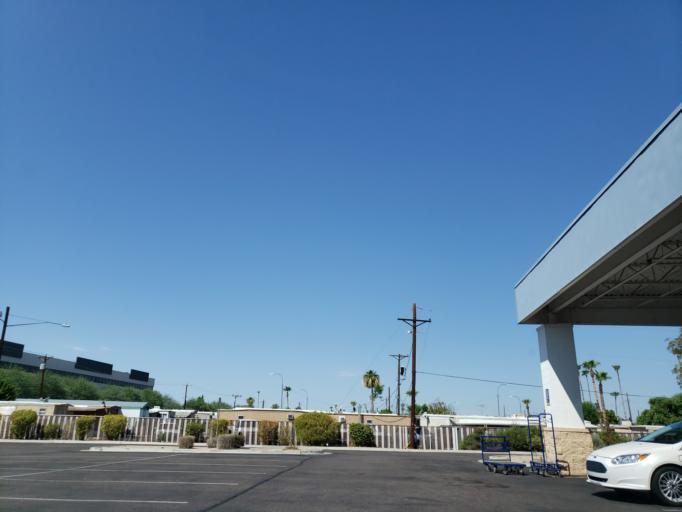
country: US
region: Arizona
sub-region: Maricopa County
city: Phoenix
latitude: 33.4918
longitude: -112.1145
